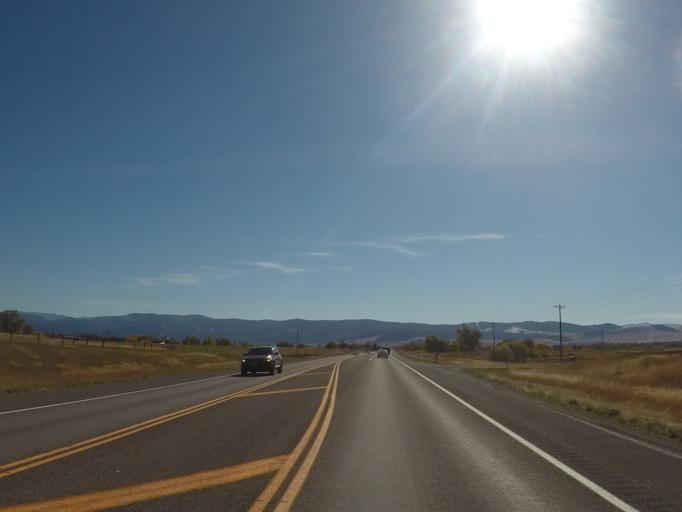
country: US
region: Montana
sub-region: Lake County
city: Ronan
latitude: 47.3583
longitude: -114.0967
